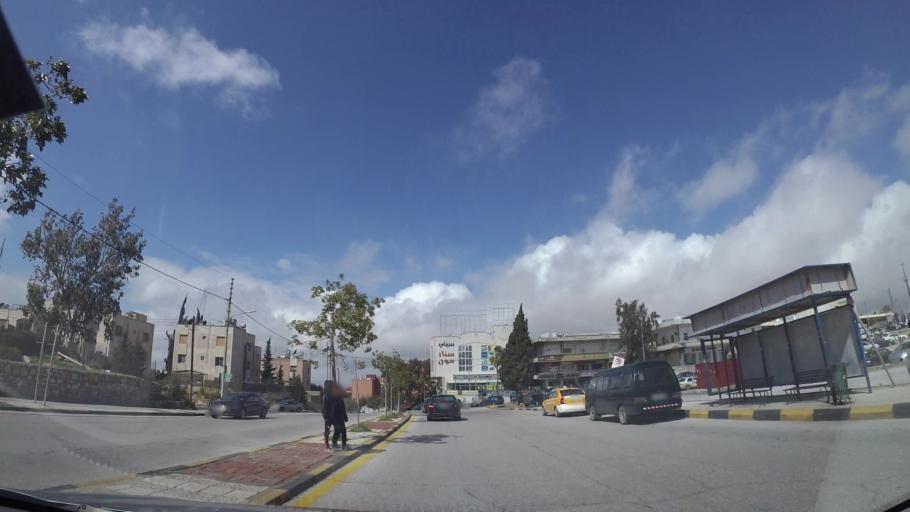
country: JO
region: Amman
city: Al Jubayhah
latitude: 32.0515
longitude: 35.8777
